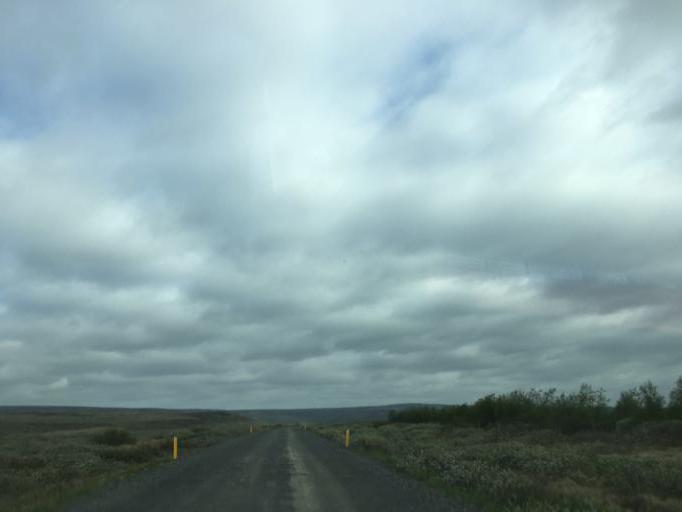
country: IS
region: South
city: Selfoss
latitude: 64.2959
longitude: -20.2384
